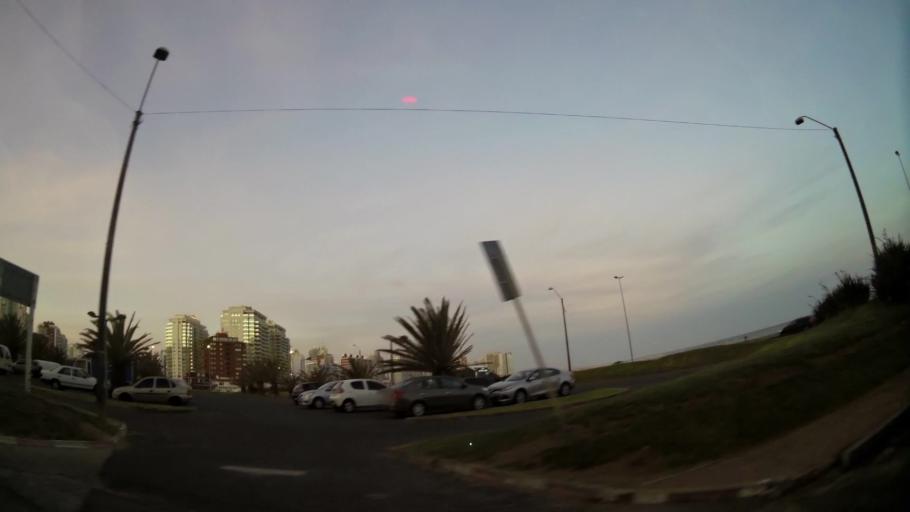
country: UY
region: Maldonado
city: Punta del Este
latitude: -34.9588
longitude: -54.9389
